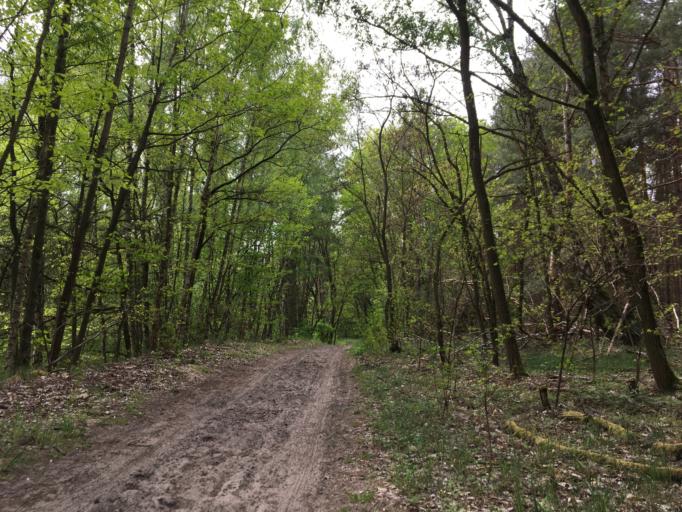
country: DE
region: Brandenburg
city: Rudnitz
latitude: 52.7035
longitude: 13.6208
